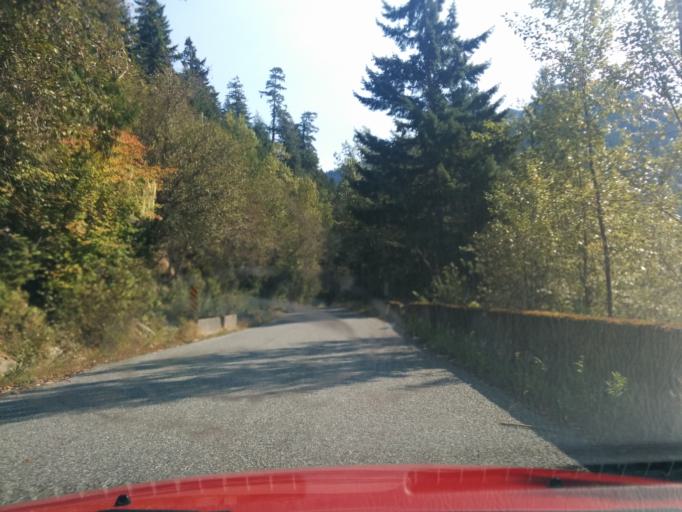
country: US
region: Washington
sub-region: Snohomish County
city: Darrington
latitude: 48.5227
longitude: -121.3759
